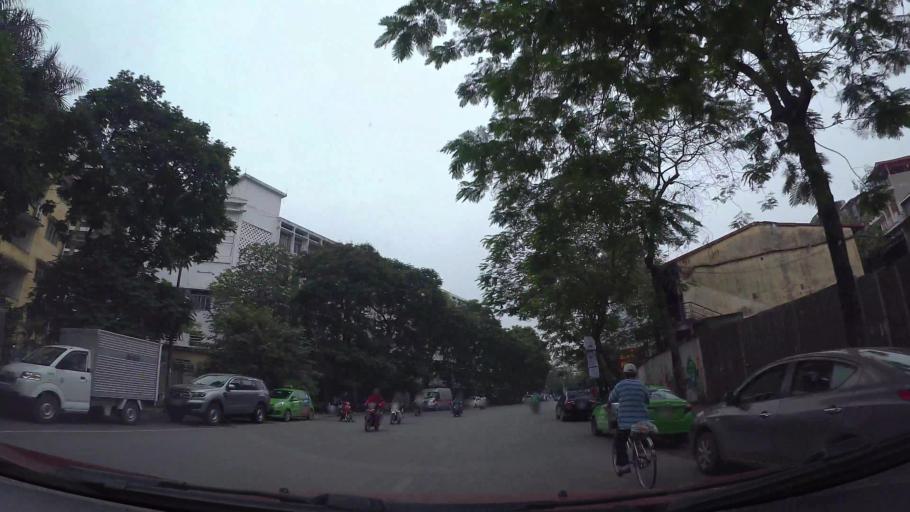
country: VN
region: Ha Noi
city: Hai BaTrung
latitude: 21.0036
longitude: 105.8448
